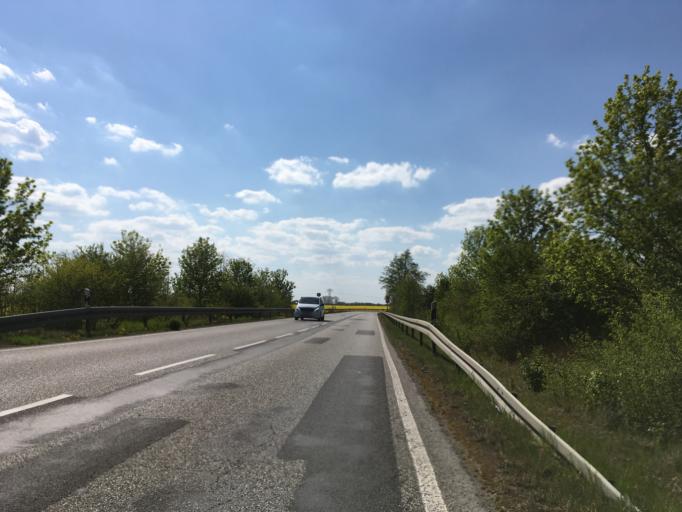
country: DE
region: Brandenburg
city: Ahrensfelde
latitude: 52.6104
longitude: 13.6524
